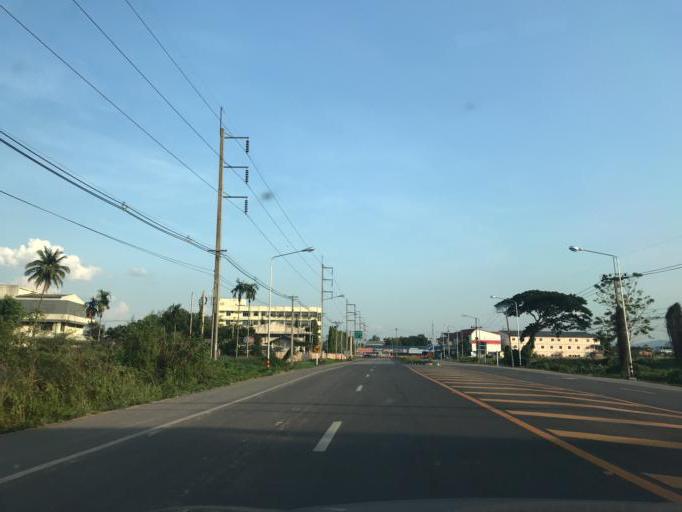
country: TH
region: Phayao
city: Chiang Kham
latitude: 19.5206
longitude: 100.2954
